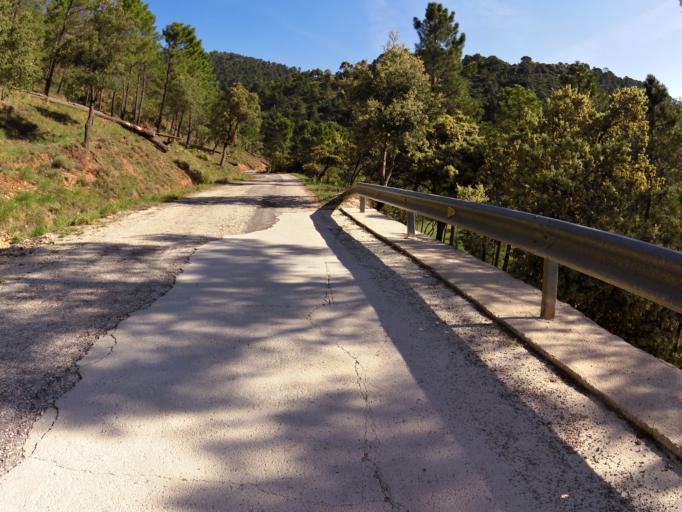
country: ES
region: Castille-La Mancha
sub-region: Provincia de Albacete
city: Riopar
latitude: 38.5216
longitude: -2.4557
